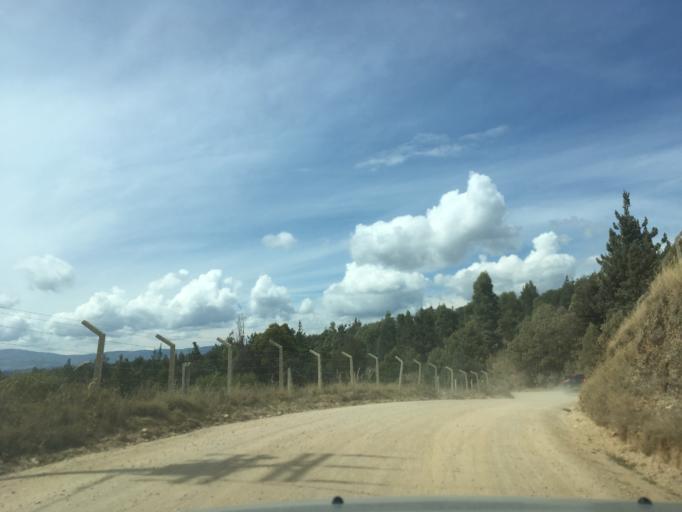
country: CO
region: Boyaca
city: Aquitania
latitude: 5.5754
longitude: -72.9416
